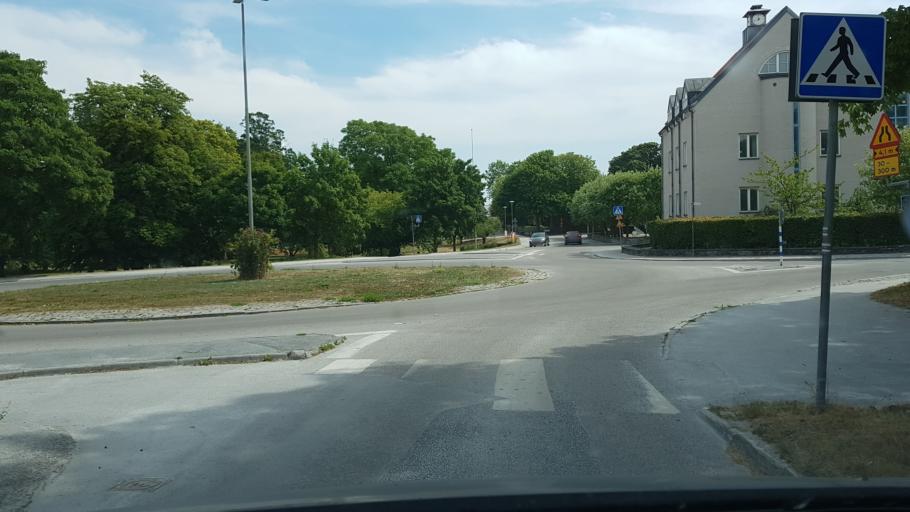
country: SE
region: Gotland
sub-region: Gotland
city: Slite
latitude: 57.7060
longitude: 18.8052
